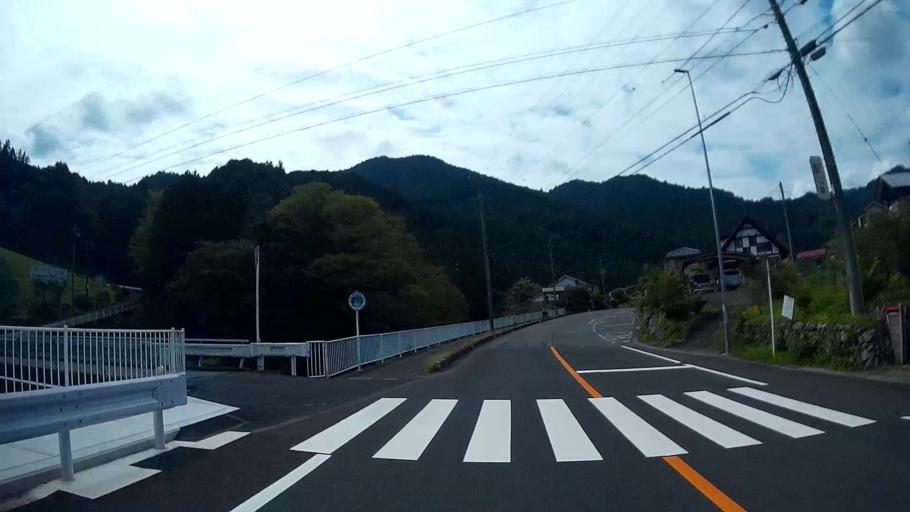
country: JP
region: Tokyo
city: Ome
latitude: 35.8537
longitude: 139.2043
